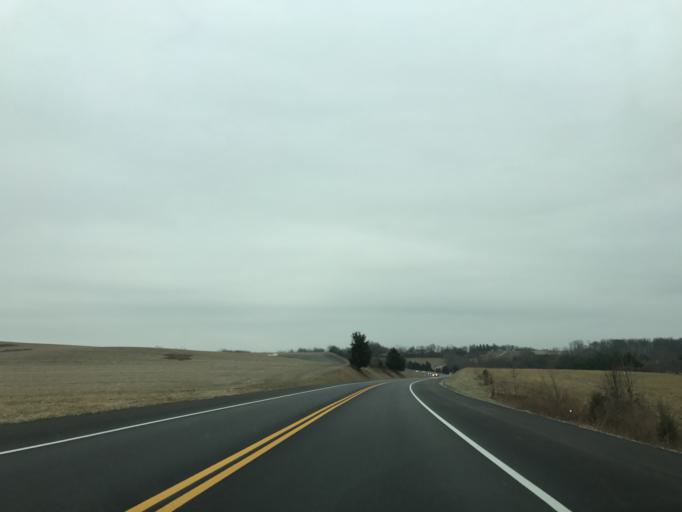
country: US
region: Maryland
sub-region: Carroll County
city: New Windsor
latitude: 39.6170
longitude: -77.0839
